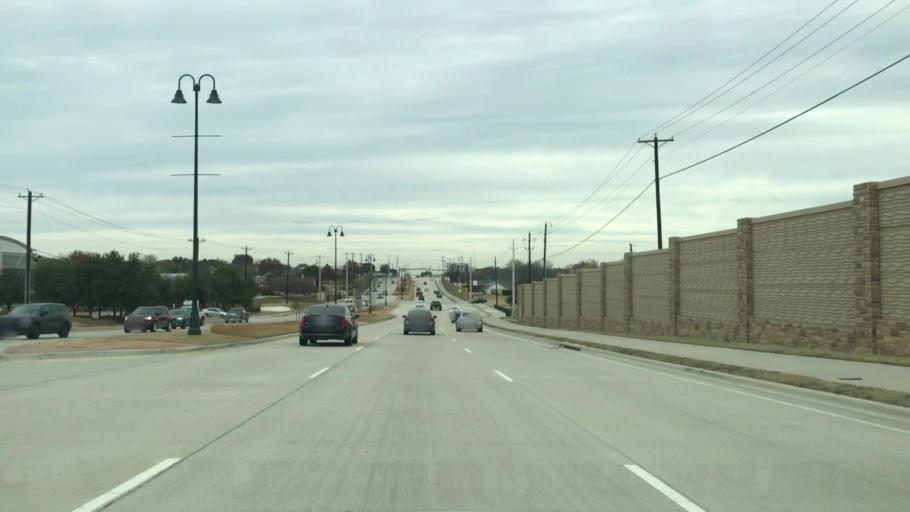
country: US
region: Texas
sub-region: Denton County
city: The Colony
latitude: 33.0902
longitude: -96.8926
